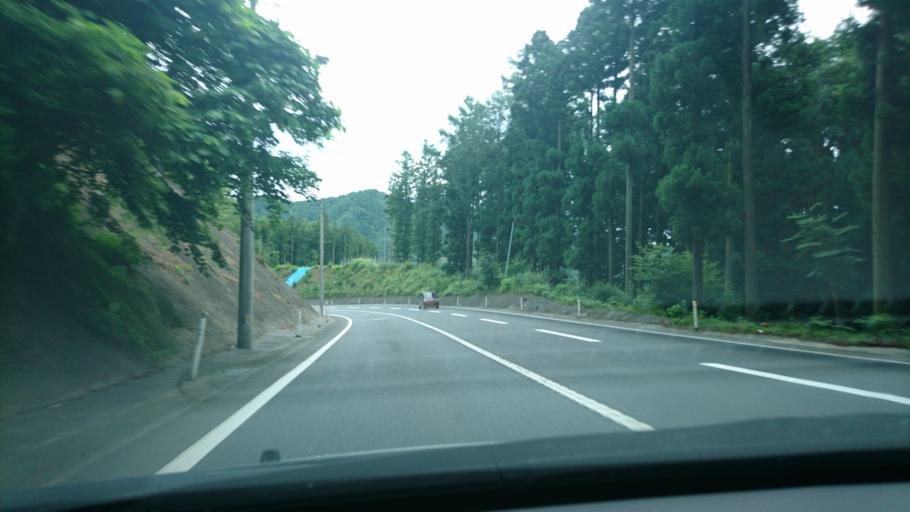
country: JP
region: Iwate
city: Kamaishi
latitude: 39.1881
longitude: 141.8495
